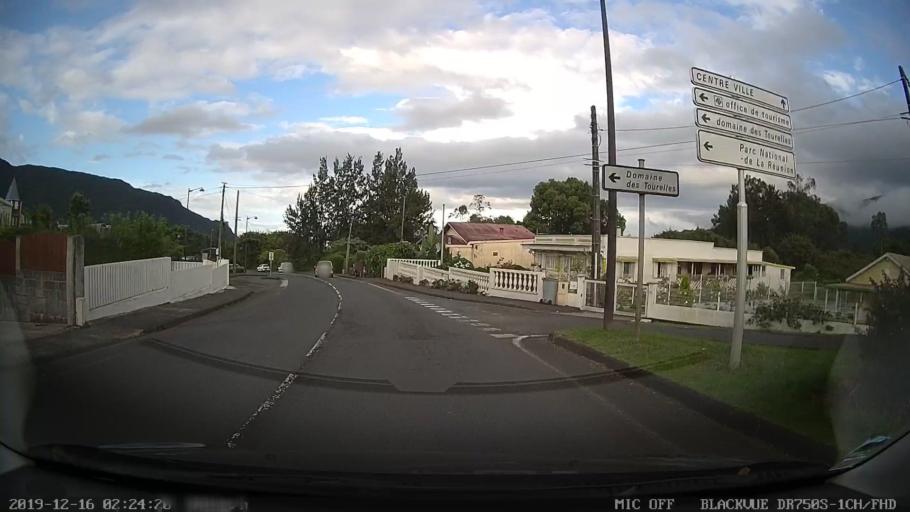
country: RE
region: Reunion
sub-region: Reunion
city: Saint-Benoit
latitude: -21.1383
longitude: 55.6239
